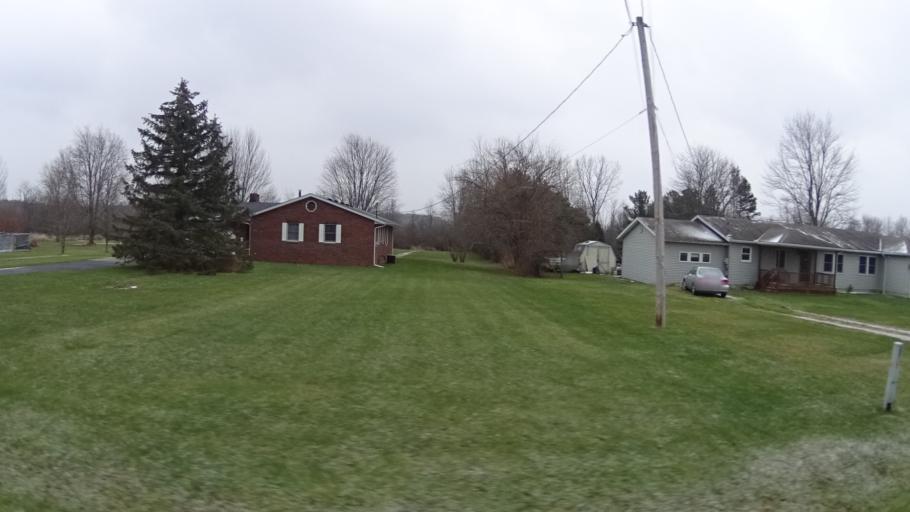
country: US
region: Ohio
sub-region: Lorain County
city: Oberlin
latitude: 41.2798
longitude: -82.2529
